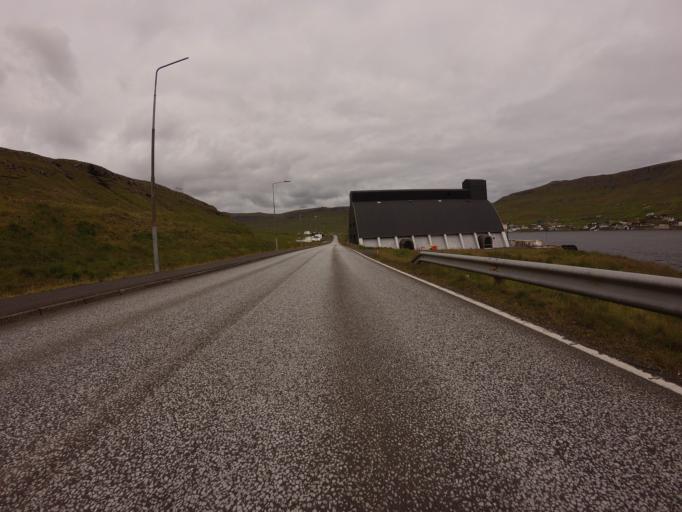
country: FO
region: Suduroy
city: Tvoroyri
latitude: 61.5513
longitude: -6.8284
